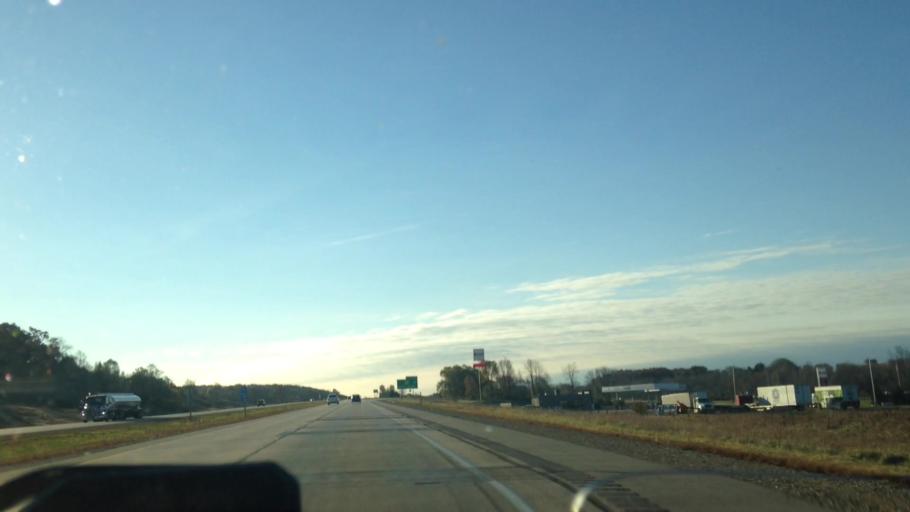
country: US
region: Wisconsin
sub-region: Washington County
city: Slinger
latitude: 43.3761
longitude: -88.3028
